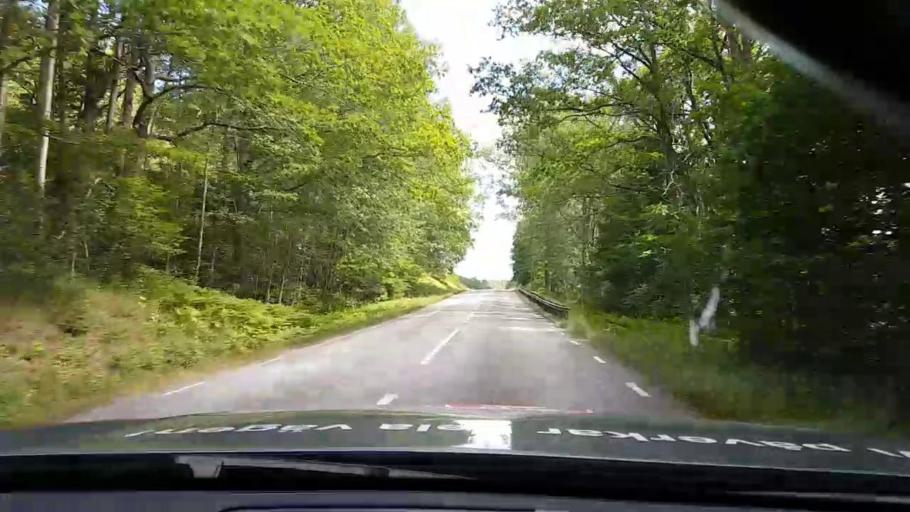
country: SE
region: Kalmar
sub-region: Vasterviks Kommun
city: Forserum
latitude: 58.0386
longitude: 16.4383
